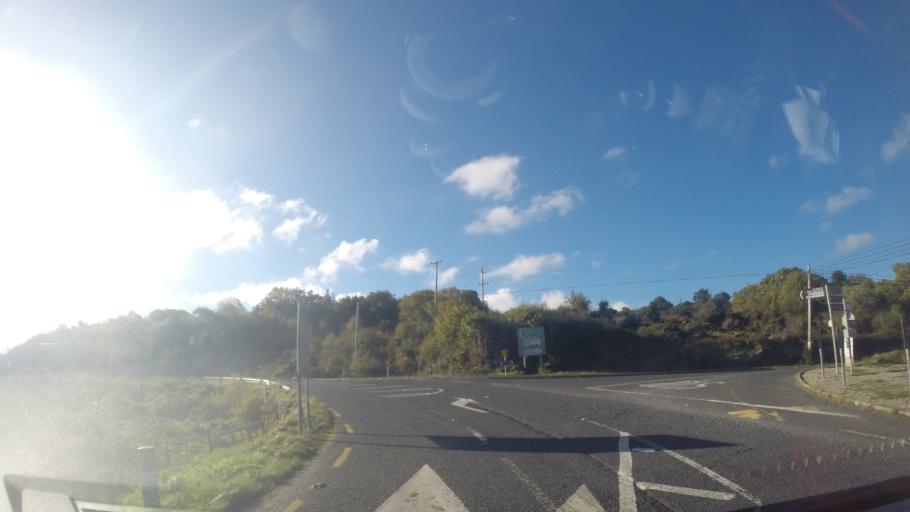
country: IE
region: Ulster
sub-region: County Donegal
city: Dungloe
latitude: 54.8308
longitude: -8.3689
